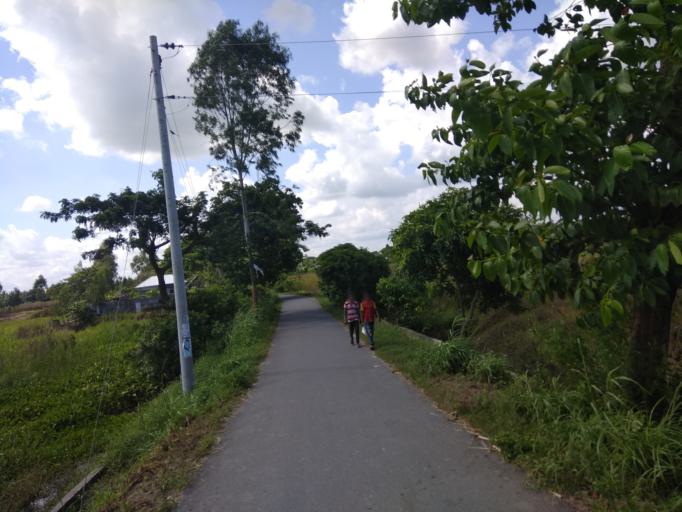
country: BD
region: Dhaka
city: Narayanganj
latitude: 23.4428
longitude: 90.4649
